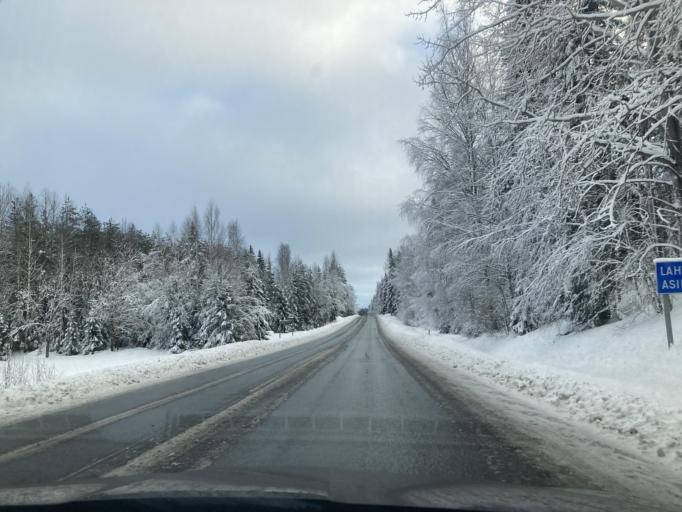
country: FI
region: Paijanne Tavastia
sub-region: Lahti
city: Padasjoki
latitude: 61.2694
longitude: 25.3298
